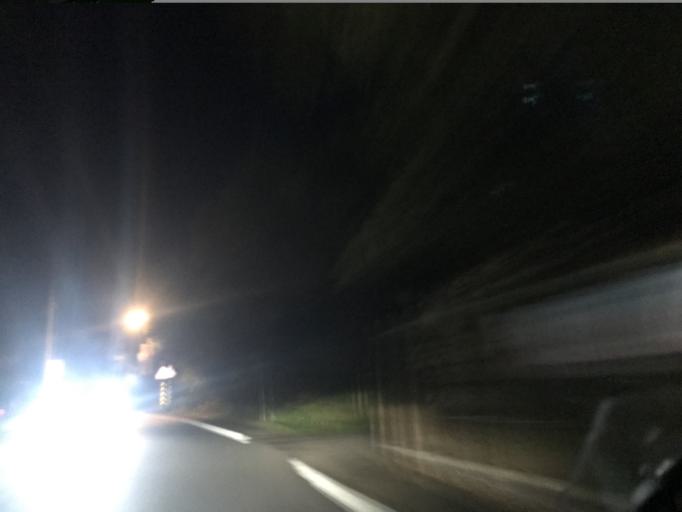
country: TW
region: Taiwan
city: Daxi
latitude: 24.8471
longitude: 121.2156
